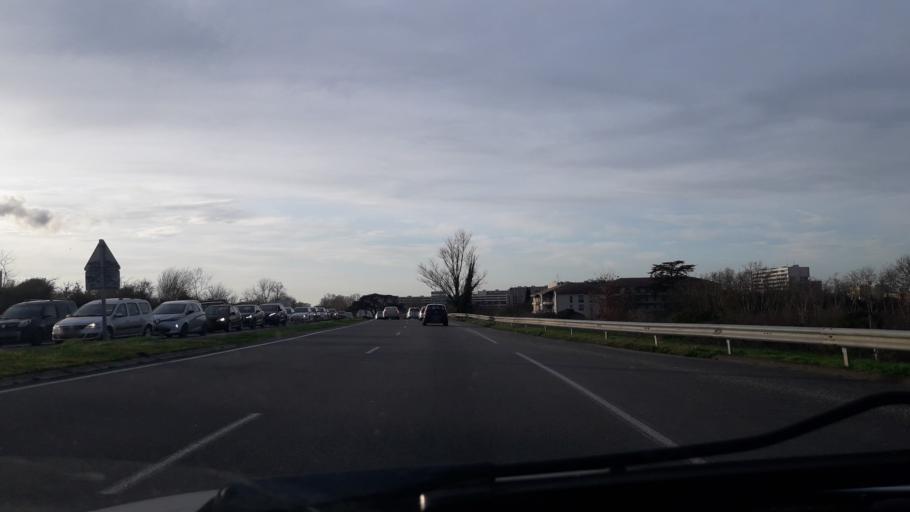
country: FR
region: Midi-Pyrenees
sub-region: Departement de la Haute-Garonne
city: Portet-sur-Garonne
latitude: 43.5571
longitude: 1.4056
